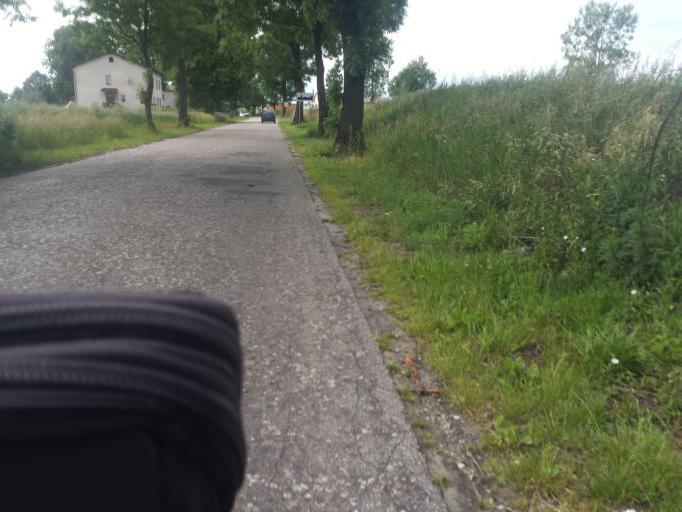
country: PL
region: Warmian-Masurian Voivodeship
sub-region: Powiat nowomiejski
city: Biskupiec
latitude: 53.5365
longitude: 19.4645
